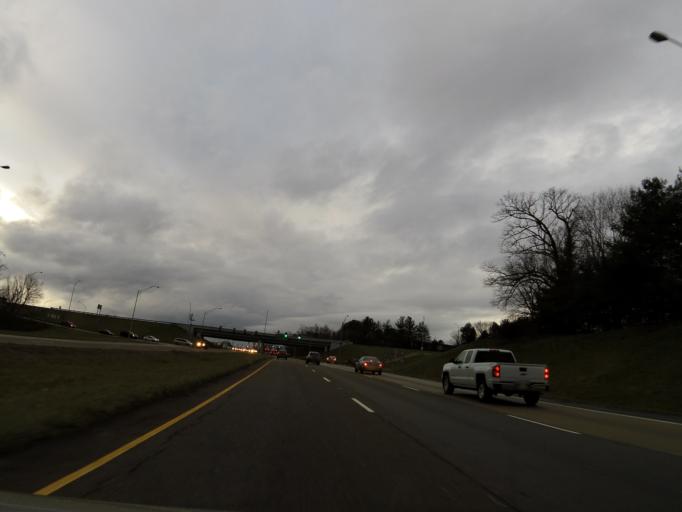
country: US
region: Tennessee
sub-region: Washington County
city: Johnson City
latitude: 36.3095
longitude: -82.3361
